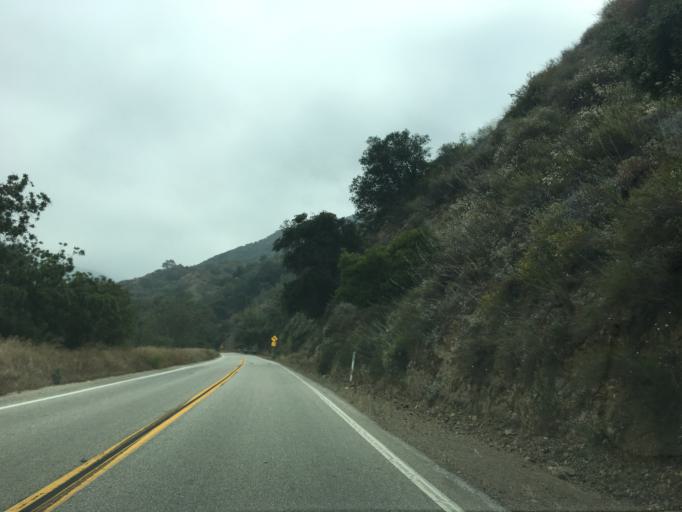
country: US
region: California
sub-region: Los Angeles County
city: Glendora
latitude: 34.1648
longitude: -117.8389
